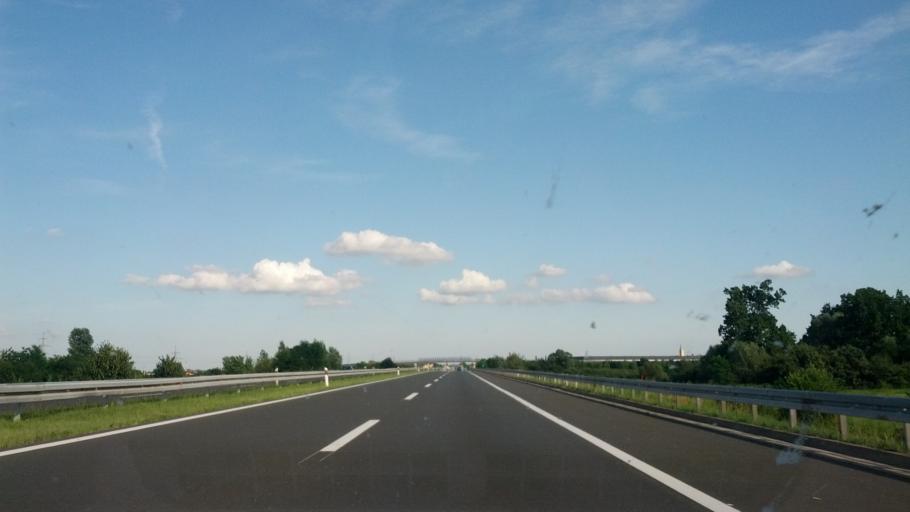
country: HR
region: Zagrebacka
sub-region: Grad Samobor
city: Samobor
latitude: 45.8110
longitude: 15.7665
